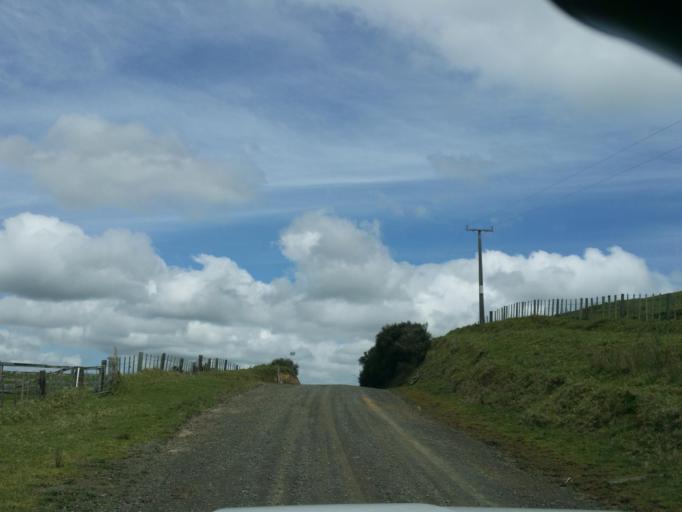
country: NZ
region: Northland
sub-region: Kaipara District
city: Dargaville
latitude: -35.9312
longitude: 174.0183
